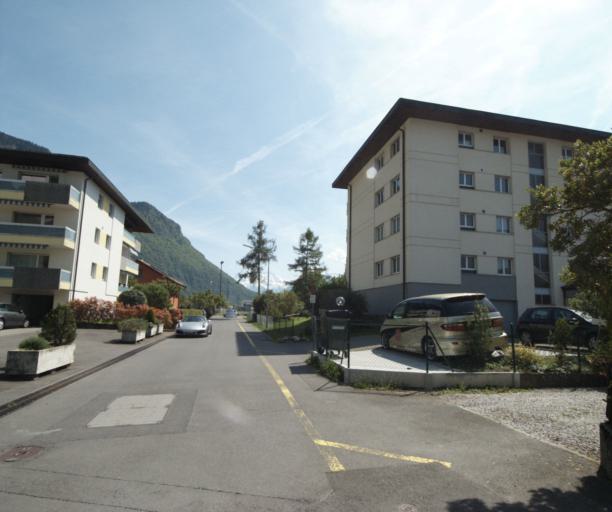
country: CH
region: Vaud
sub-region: Aigle District
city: Villeneuve
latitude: 46.3933
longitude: 6.9256
